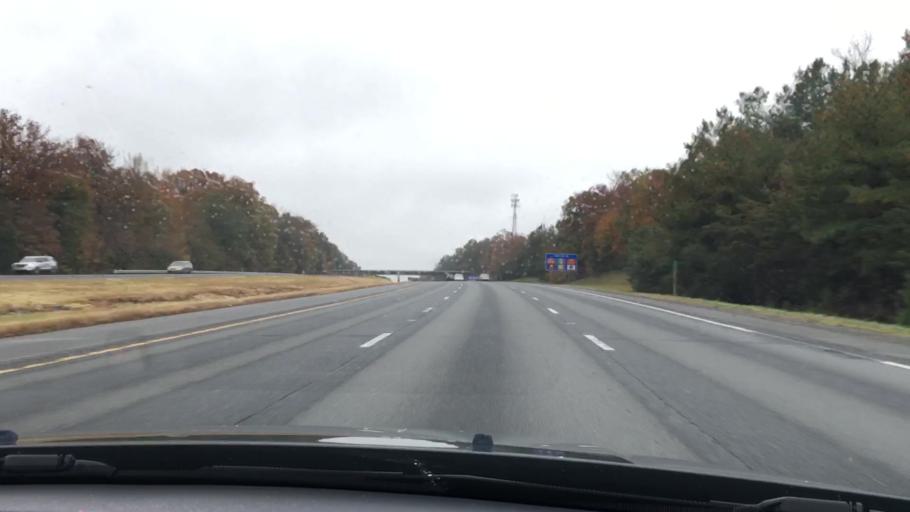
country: US
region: Virginia
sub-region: Spotsylvania County
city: Spotsylvania Courthouse
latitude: 38.1590
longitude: -77.5077
